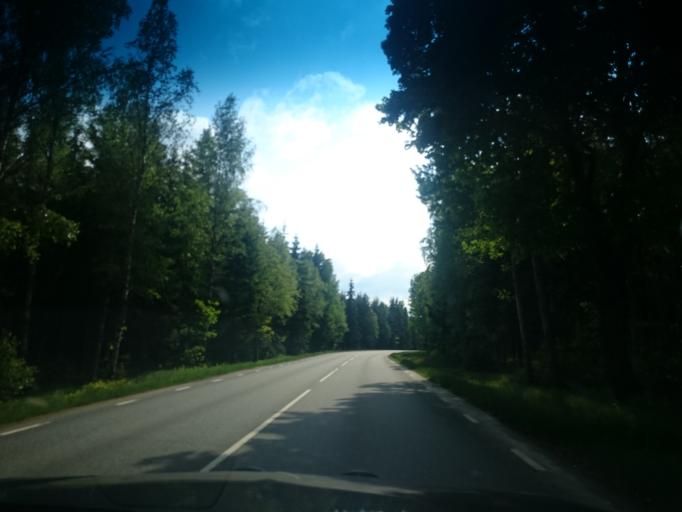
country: SE
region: Joenkoeping
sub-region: Vetlanda Kommun
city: Vetlanda
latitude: 57.4041
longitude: 14.9975
